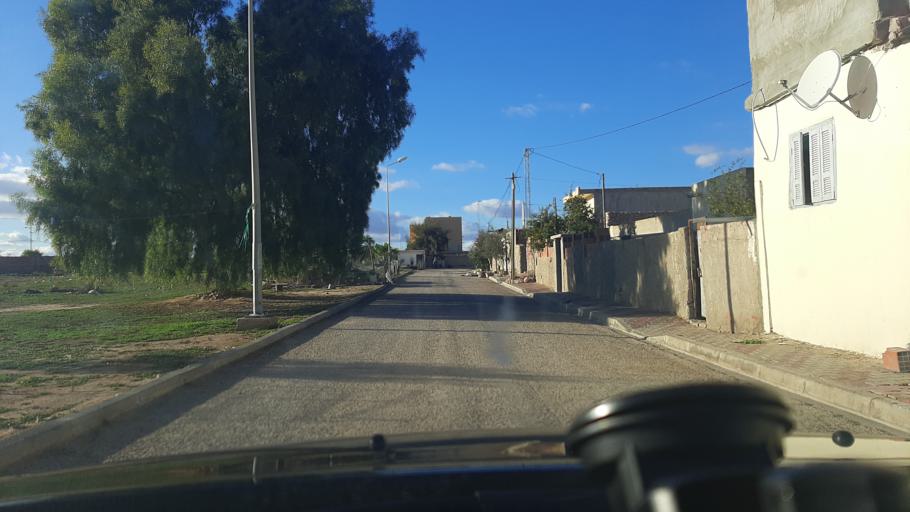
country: TN
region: Al Mahdiyah
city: Shurban
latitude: 34.9596
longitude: 10.3638
